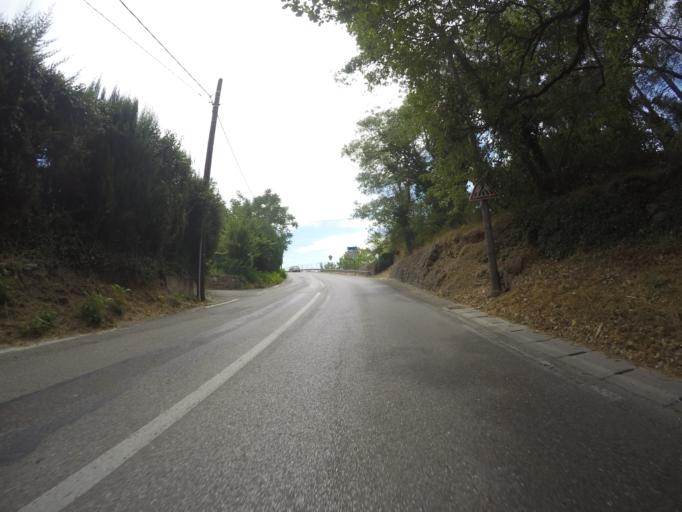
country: FR
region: Provence-Alpes-Cote d'Azur
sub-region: Departement des Alpes-Maritimes
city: Mougins
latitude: 43.6060
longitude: 6.9988
